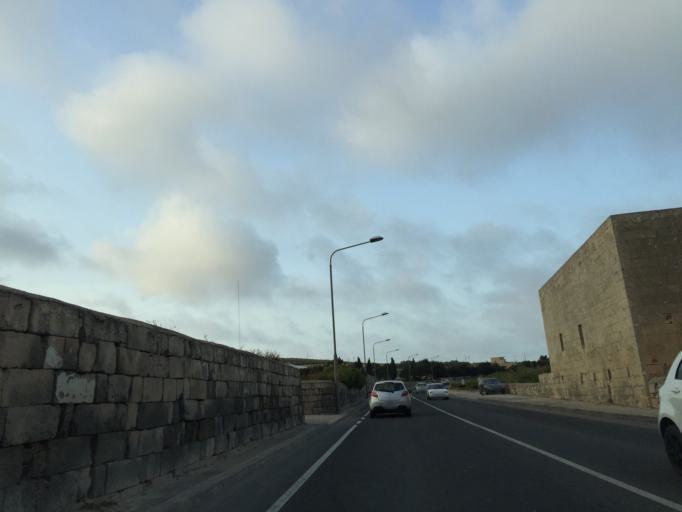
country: MT
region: Il-Mosta
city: Mosta
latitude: 35.9086
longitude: 14.4104
